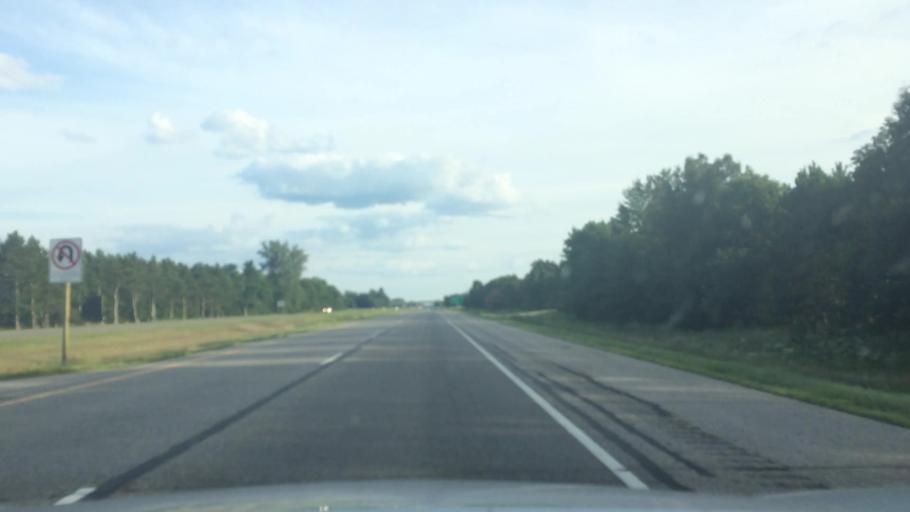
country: US
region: Wisconsin
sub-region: Portage County
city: Plover
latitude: 44.3181
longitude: -89.5236
